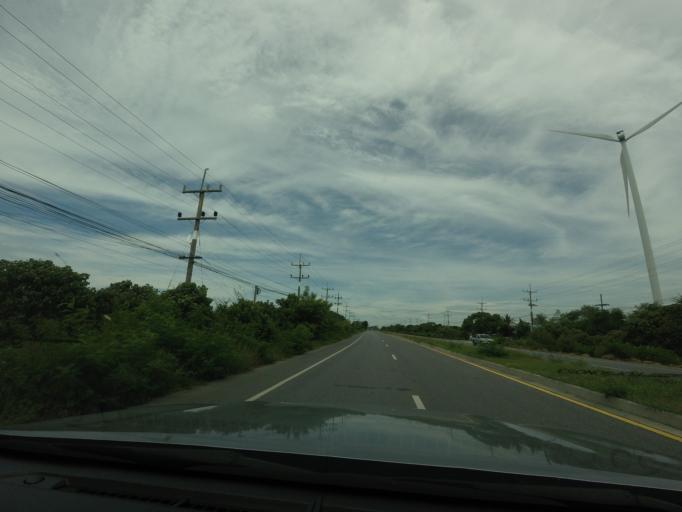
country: TH
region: Songkhla
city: Ranot
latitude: 7.8257
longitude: 100.3565
